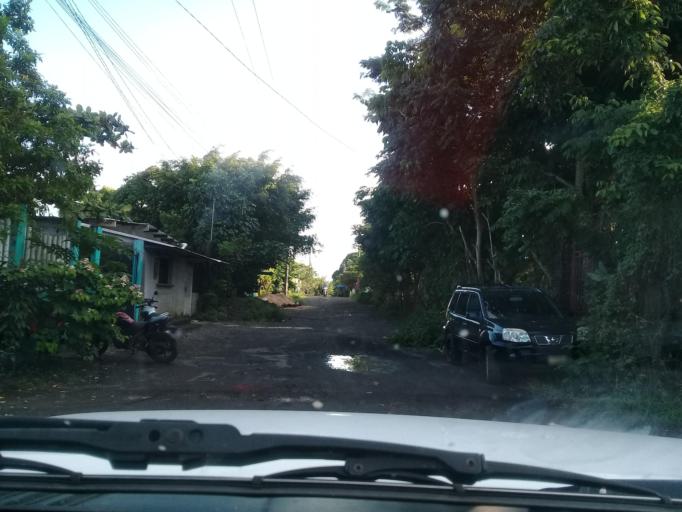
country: MX
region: Veracruz
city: Catemaco
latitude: 18.4248
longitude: -95.1012
